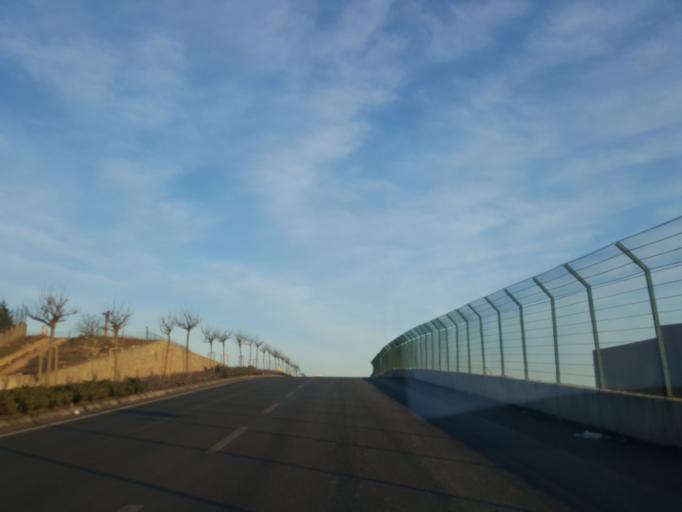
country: TR
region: Kocaeli
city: Tavsanli
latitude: 40.8209
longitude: 29.5608
